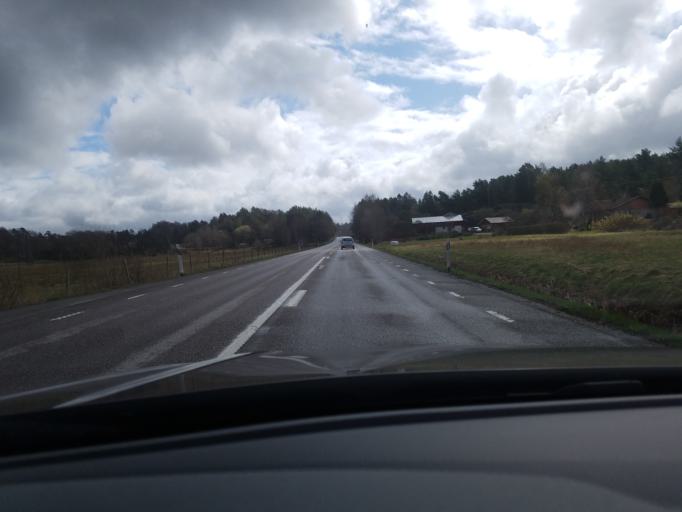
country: SE
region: Vaestra Goetaland
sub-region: Tjorns Kommun
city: Myggenas
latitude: 58.0662
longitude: 11.7099
